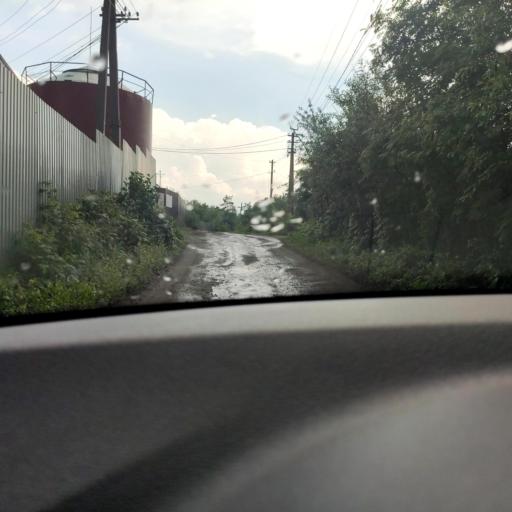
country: RU
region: Samara
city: Novosemeykino
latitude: 53.3997
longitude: 50.3135
